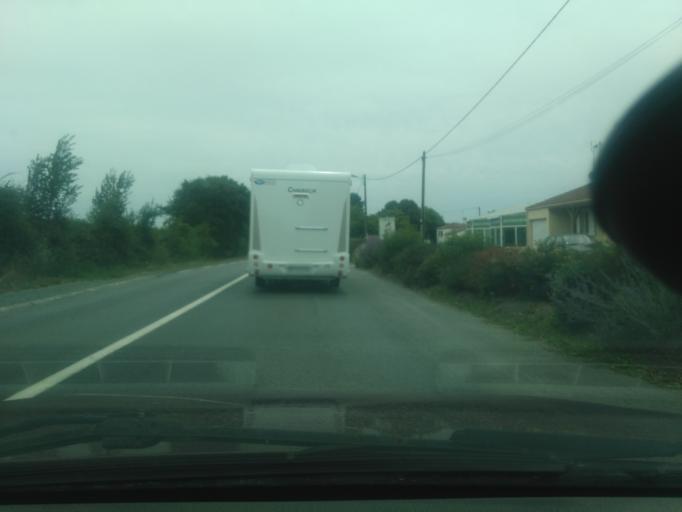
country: FR
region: Pays de la Loire
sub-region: Departement de la Vendee
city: Sainte-Cecile
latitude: 46.7380
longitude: -1.0845
